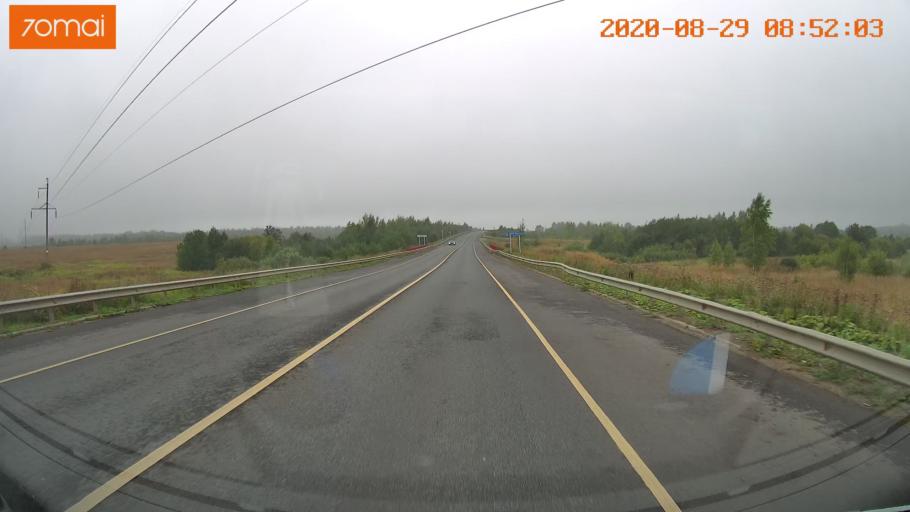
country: RU
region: Ivanovo
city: Vichuga
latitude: 57.2042
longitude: 41.8708
